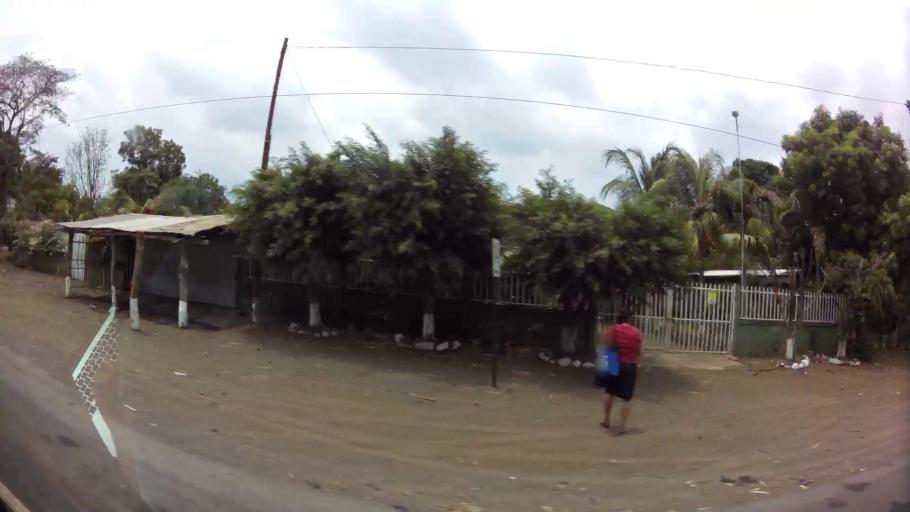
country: NI
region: Leon
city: Telica
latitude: 12.5274
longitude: -86.8821
